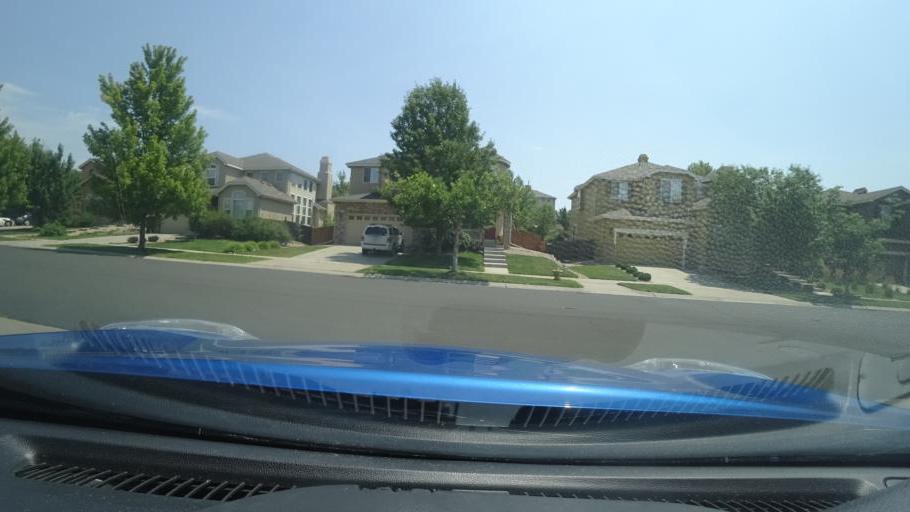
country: US
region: Colorado
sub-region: Adams County
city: Aurora
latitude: 39.6737
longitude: -104.7589
